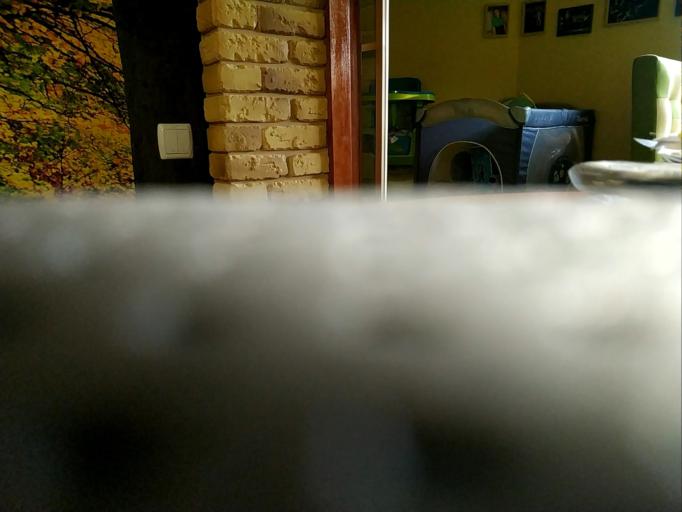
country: RU
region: Kaluga
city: Seredeyskiy
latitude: 53.8649
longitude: 35.3688
